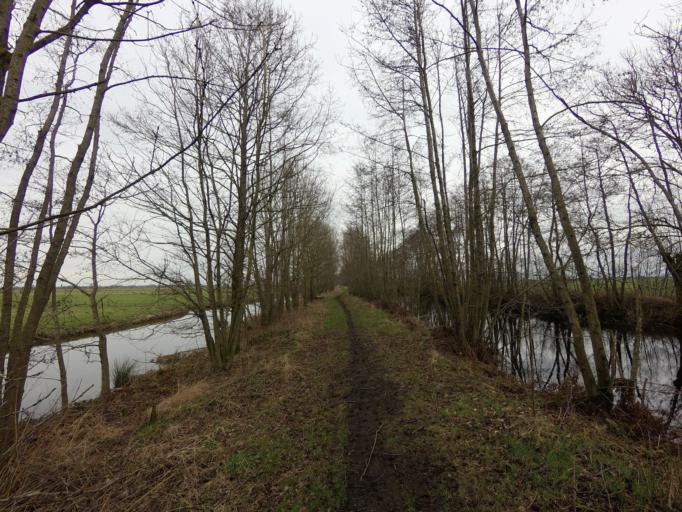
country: NL
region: Utrecht
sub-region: Gemeente Oudewater
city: Oudewater
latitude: 51.9928
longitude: 4.8566
